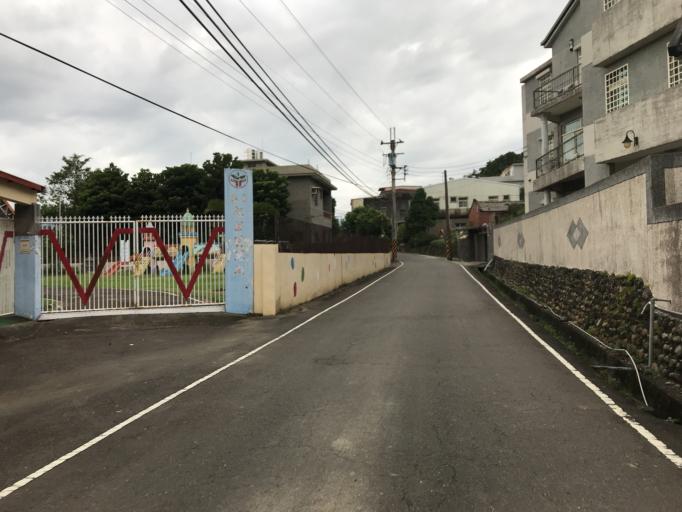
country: TW
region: Taiwan
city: Daxi
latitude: 24.7827
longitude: 121.1752
